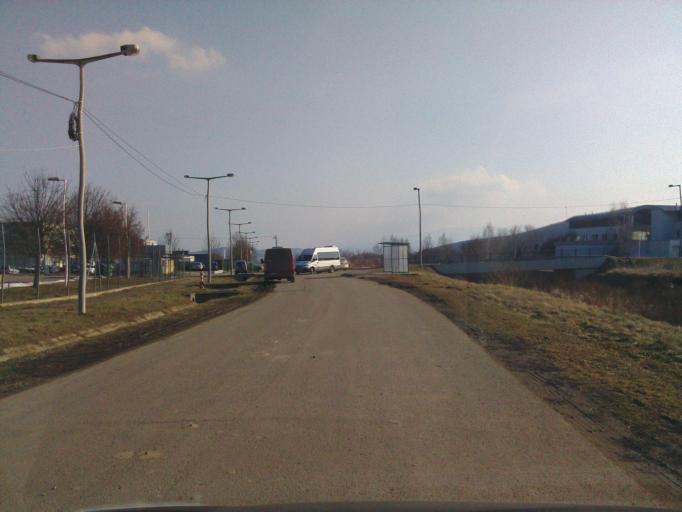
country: HU
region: Nograd
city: Salgotarjan
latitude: 48.0450
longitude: 19.7932
